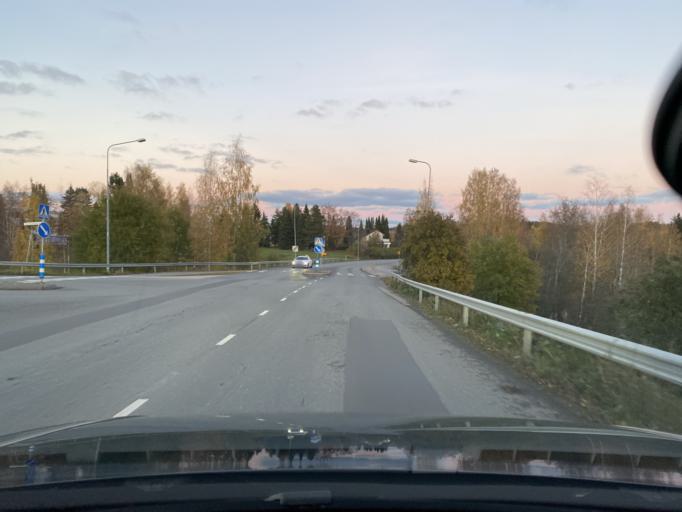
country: FI
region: Pirkanmaa
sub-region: Tampere
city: Lempaeaelae
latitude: 61.3277
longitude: 23.7602
